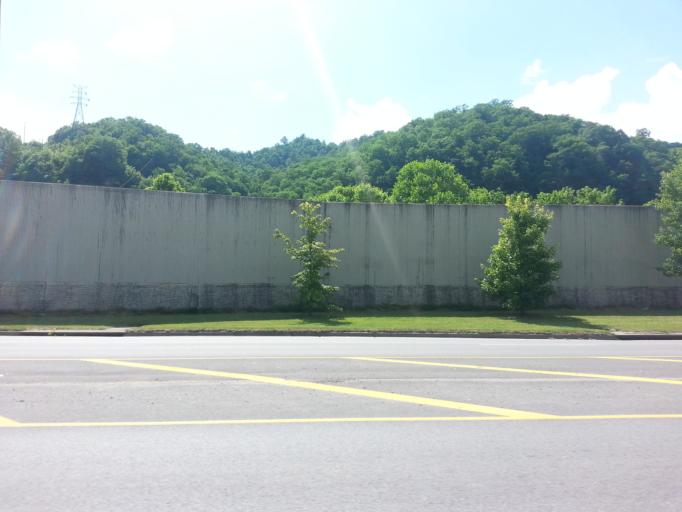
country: US
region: Kentucky
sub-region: Harlan County
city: Harlan
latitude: 36.8437
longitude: -83.3246
